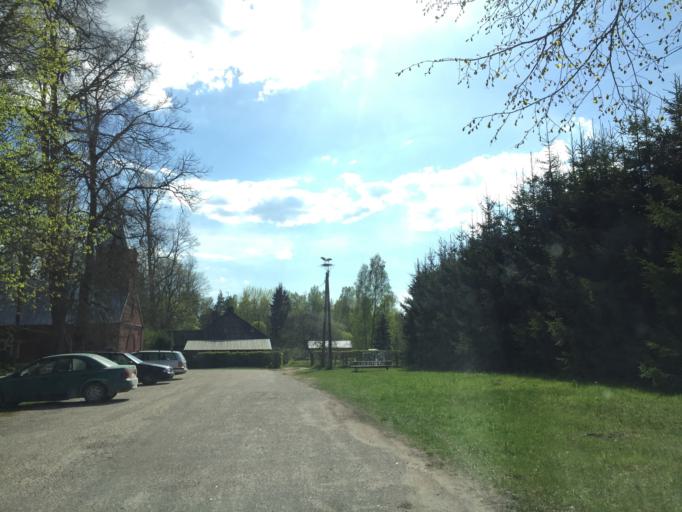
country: LV
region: Limbazu Rajons
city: Limbazi
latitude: 57.5091
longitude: 24.8193
